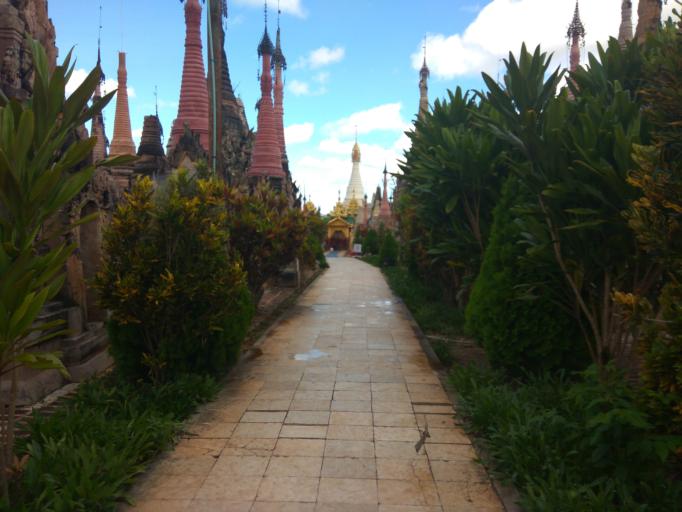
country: MM
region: Shan
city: Taunggyi
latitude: 20.4453
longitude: 97.1384
